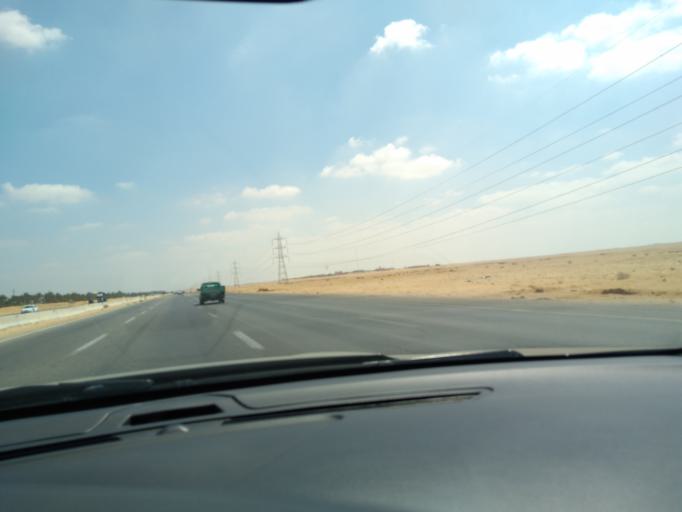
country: EG
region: Al Isma'iliyah
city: At Tall al Kabir
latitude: 30.3832
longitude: 31.9508
